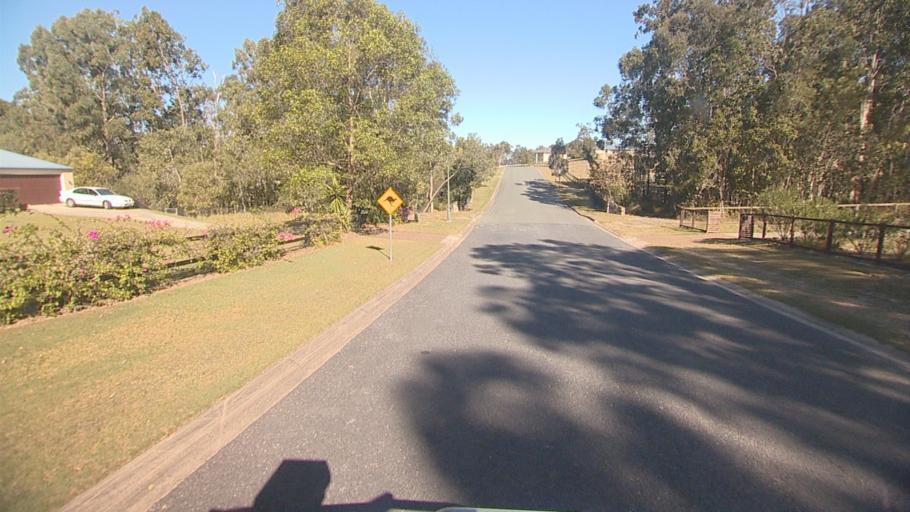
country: AU
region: Queensland
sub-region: Ipswich
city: Springfield Lakes
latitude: -27.7380
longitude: 152.9191
